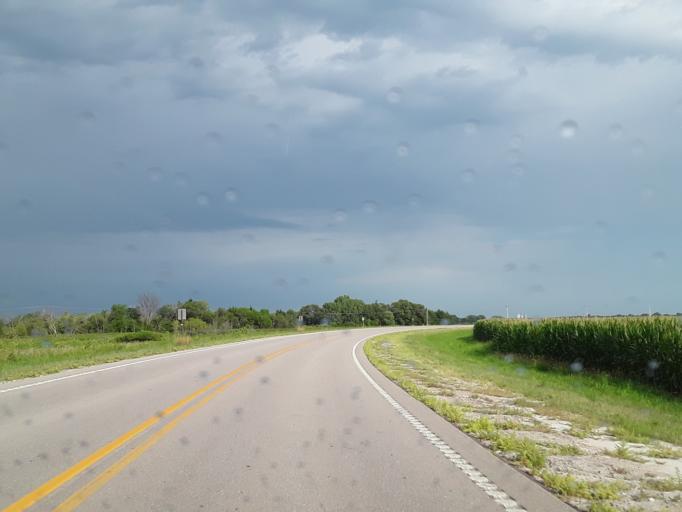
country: US
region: Nebraska
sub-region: Saunders County
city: Ashland
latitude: 41.0881
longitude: -96.3725
